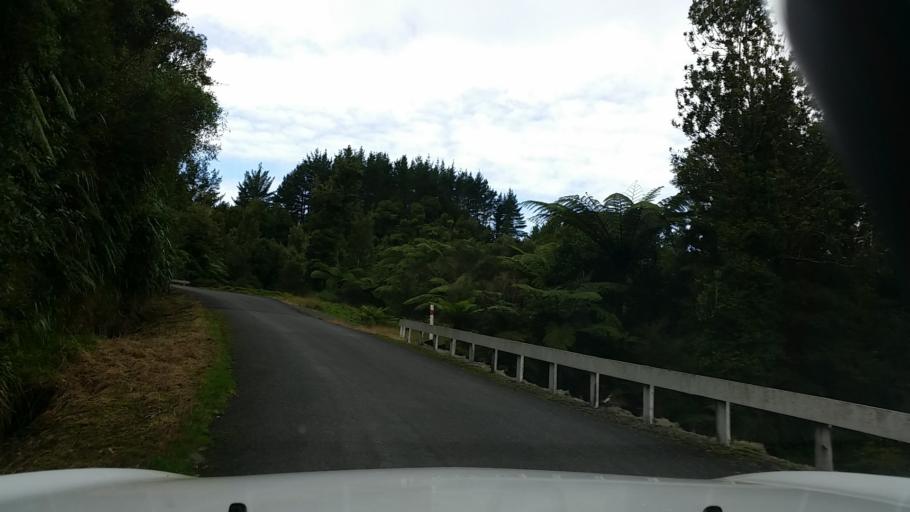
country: NZ
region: Taranaki
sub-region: New Plymouth District
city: Waitara
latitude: -38.9142
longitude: 174.7639
